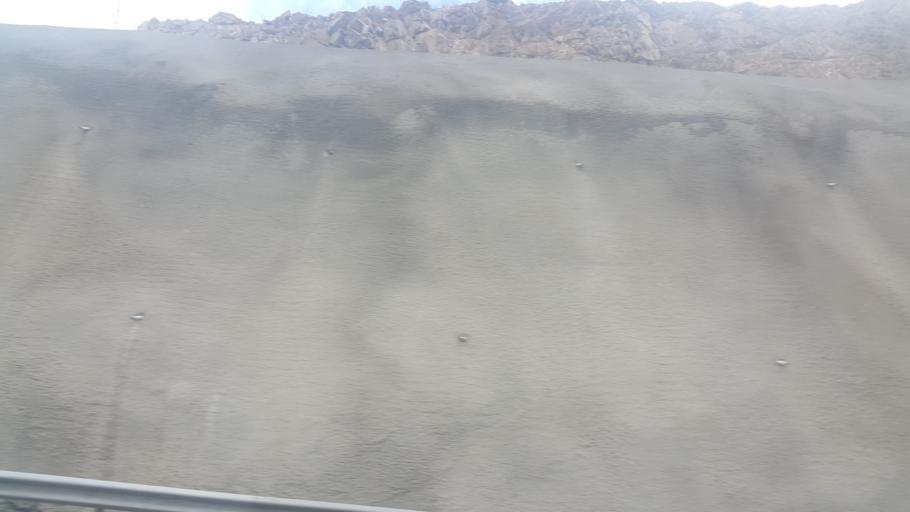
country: TR
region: Nigde
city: Ciftehan
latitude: 37.5310
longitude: 34.8102
